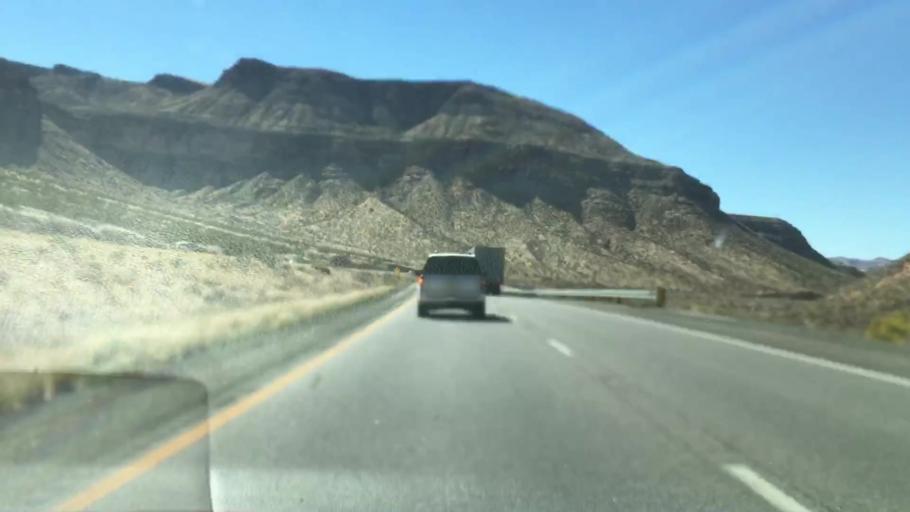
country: US
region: Utah
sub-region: Washington County
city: Santa Clara
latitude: 36.9747
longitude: -113.6846
